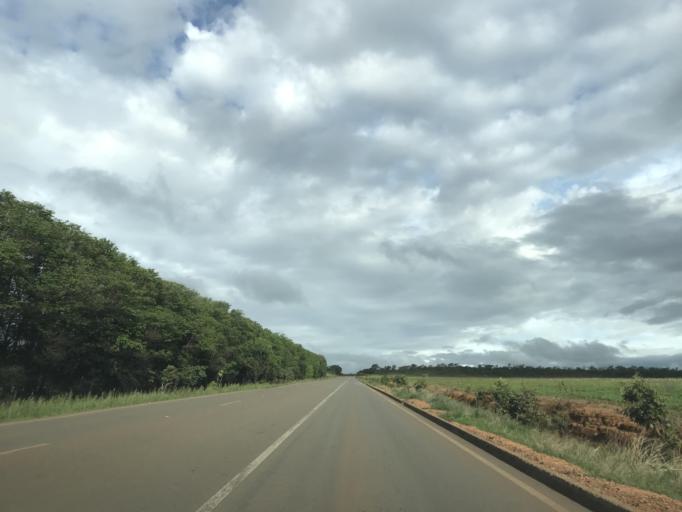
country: BR
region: Goias
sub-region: Vianopolis
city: Vianopolis
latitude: -16.5767
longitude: -48.3037
